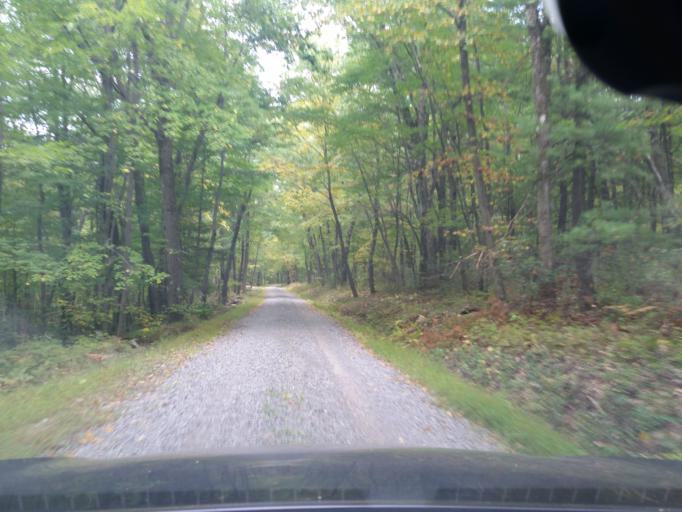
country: US
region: Pennsylvania
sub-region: Lycoming County
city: Jersey Shore
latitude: 41.0870
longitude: -77.1910
